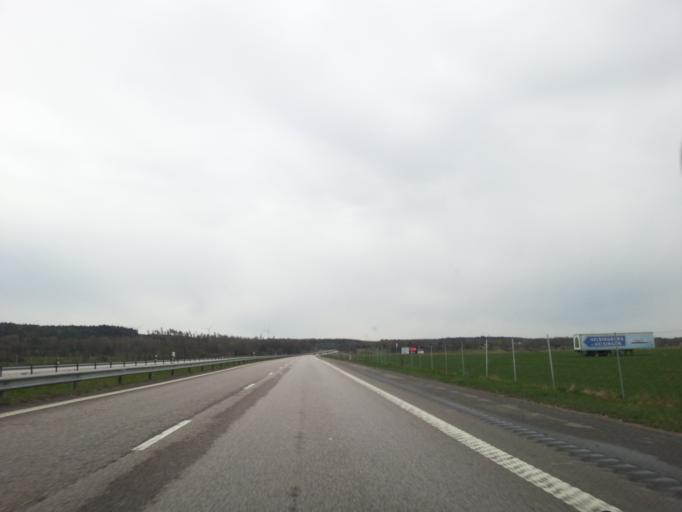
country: SE
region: Halland
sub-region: Varbergs Kommun
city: Veddige
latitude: 57.2278
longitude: 12.2294
